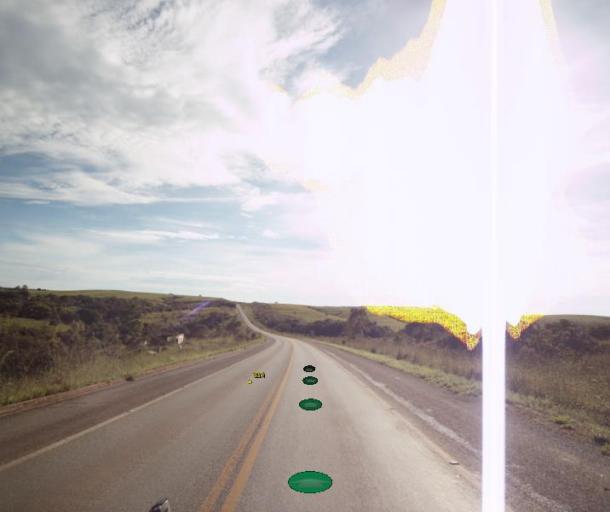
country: BR
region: Goias
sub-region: Abadiania
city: Abadiania
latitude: -15.7833
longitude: -48.4744
